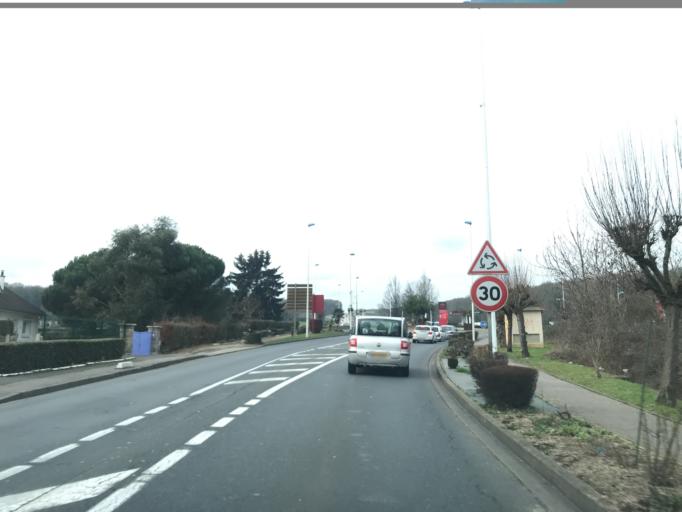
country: FR
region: Haute-Normandie
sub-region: Departement de l'Eure
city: Fleury-sur-Andelle
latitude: 49.3645
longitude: 1.3513
